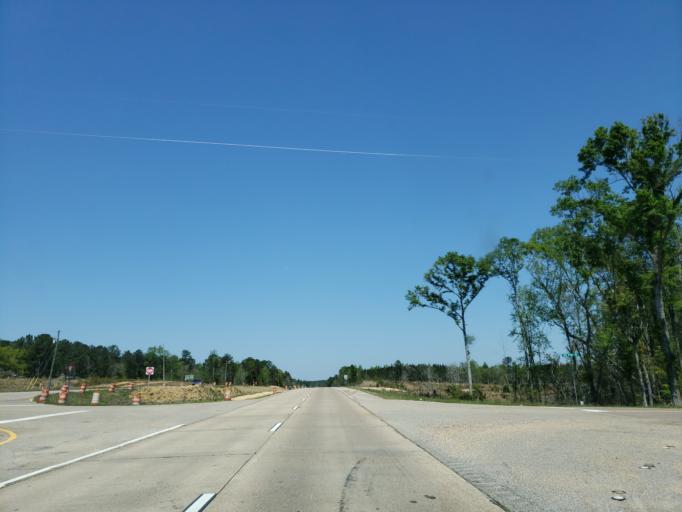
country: US
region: Mississippi
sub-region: Lamar County
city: Purvis
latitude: 31.0834
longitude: -89.2117
